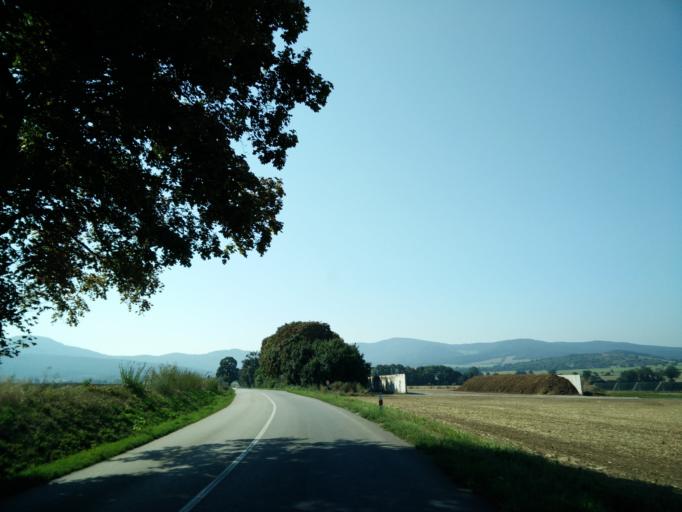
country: SK
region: Nitriansky
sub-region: Okres Nitra
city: Nitra
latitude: 48.4096
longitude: 18.1167
